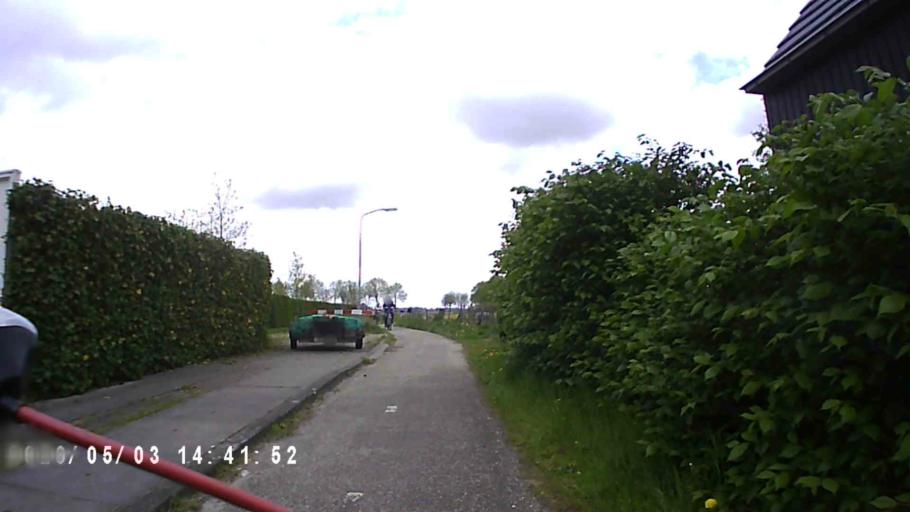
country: NL
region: Groningen
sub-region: Gemeente De Marne
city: Ulrum
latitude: 53.3613
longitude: 6.3854
